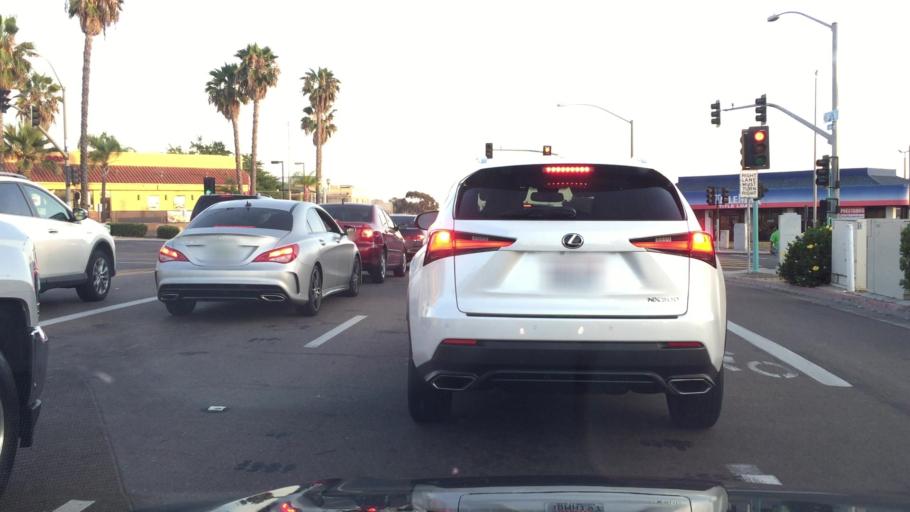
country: US
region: California
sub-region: San Diego County
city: Lemon Grove
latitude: 32.7582
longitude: -117.0795
